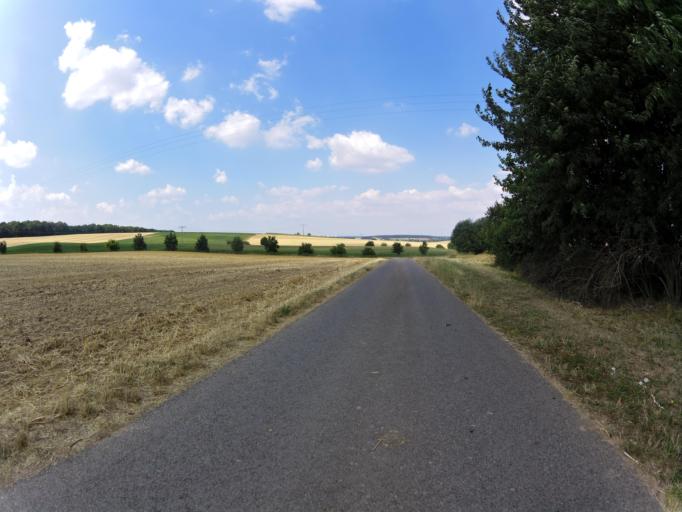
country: DE
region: Bavaria
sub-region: Regierungsbezirk Unterfranken
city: Ochsenfurt
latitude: 49.6411
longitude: 10.0566
